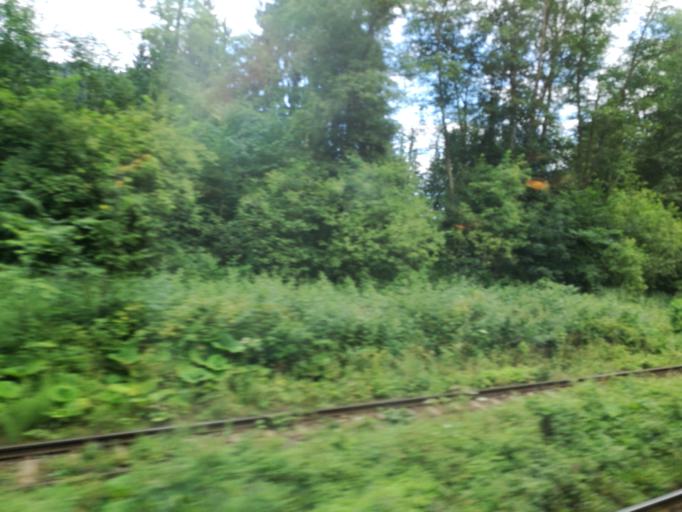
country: RO
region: Brasov
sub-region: Oras Predeal
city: Predeal
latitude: 45.5534
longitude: 25.5892
